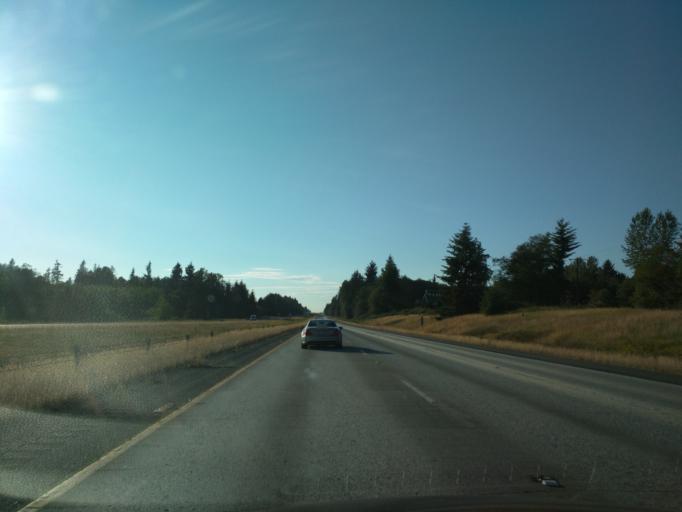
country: US
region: Washington
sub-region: Snohomish County
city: Stanwood
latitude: 48.2780
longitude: -122.2806
